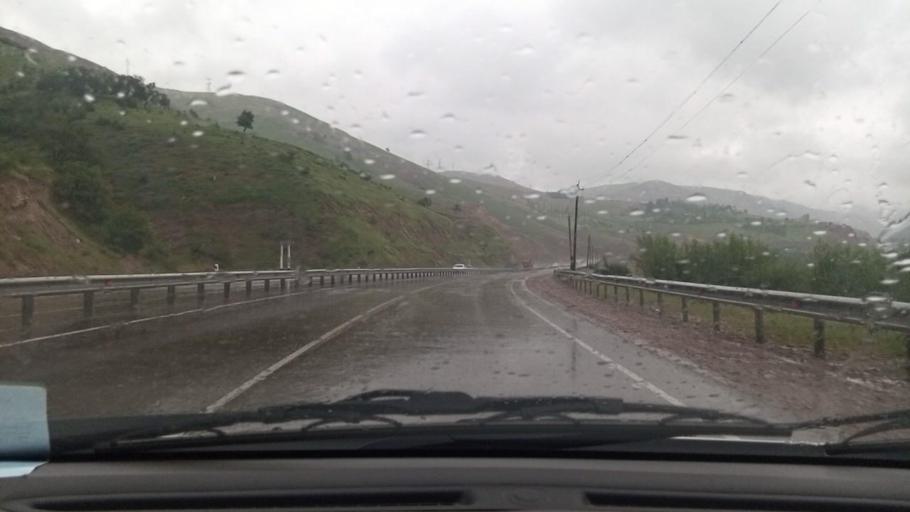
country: UZ
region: Toshkent
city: Angren
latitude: 41.0920
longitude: 70.3197
